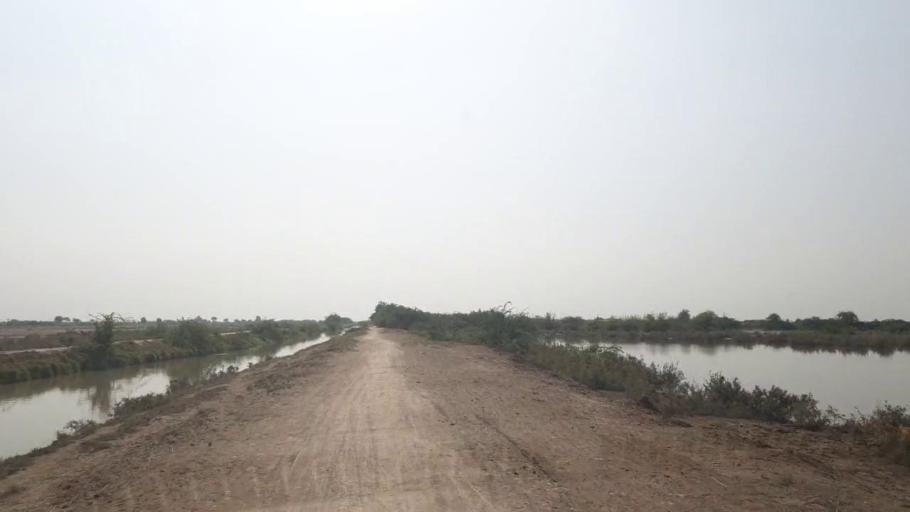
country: PK
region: Sindh
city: Kadhan
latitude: 24.5092
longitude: 68.8503
